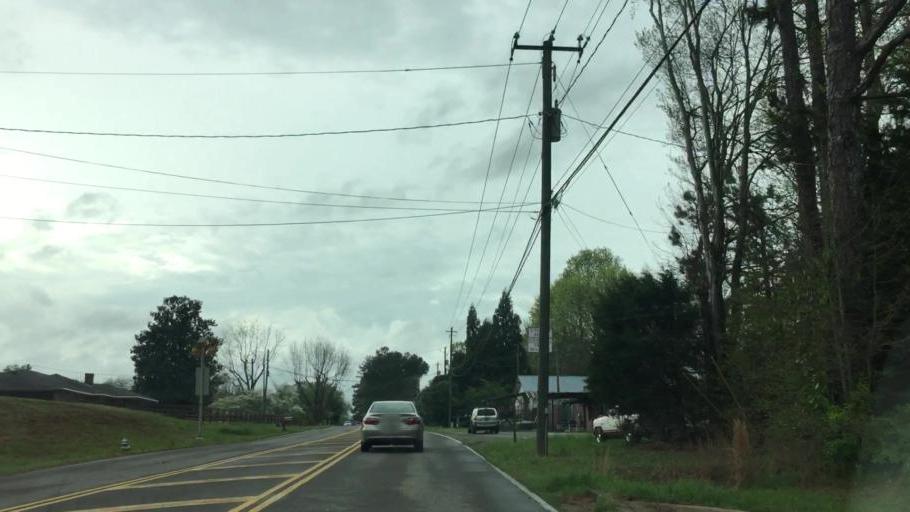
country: US
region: Georgia
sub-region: Cherokee County
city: Canton
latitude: 34.2143
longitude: -84.3984
